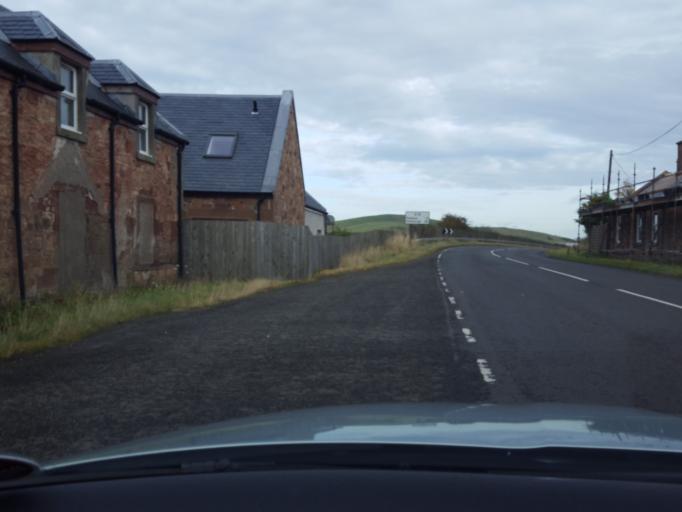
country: GB
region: Scotland
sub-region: The Scottish Borders
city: West Linton
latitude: 55.6849
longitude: -3.3986
